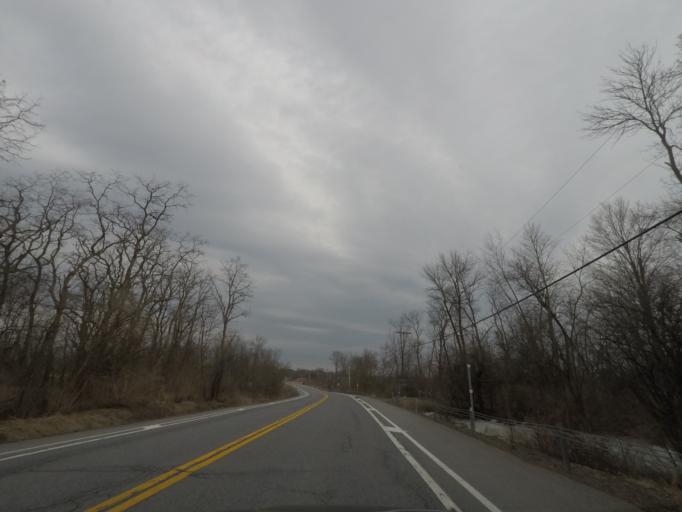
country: US
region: New York
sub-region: Washington County
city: Fort Edward
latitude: 43.2320
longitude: -73.5885
